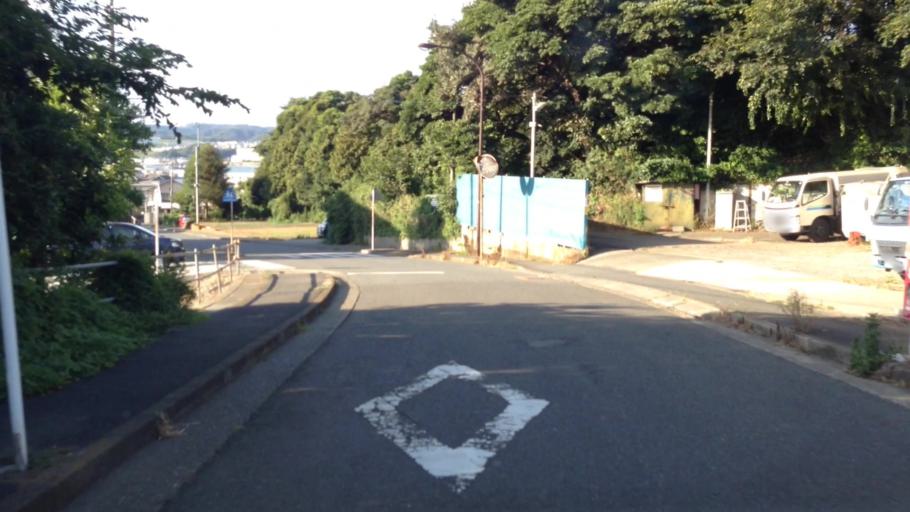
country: JP
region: Kanagawa
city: Miura
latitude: 35.2052
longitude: 139.6156
